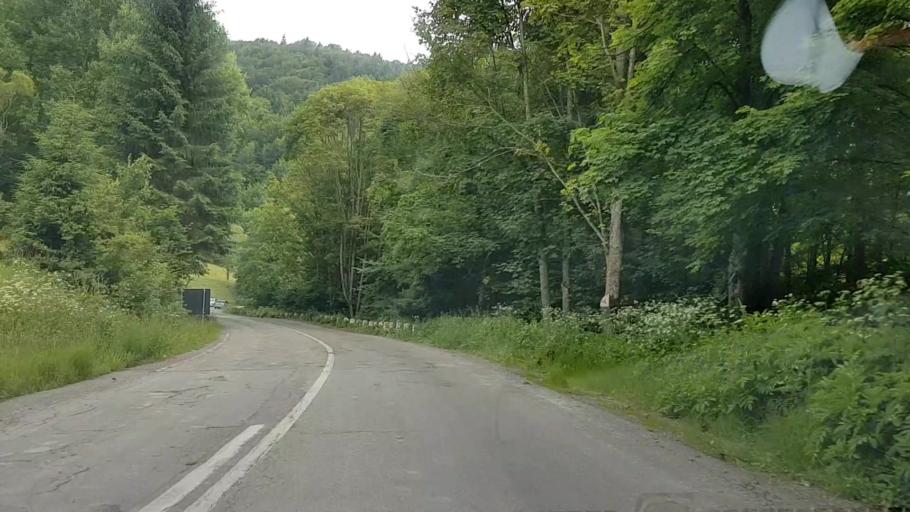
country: RO
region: Neamt
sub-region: Comuna Pangarati
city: Pangarati
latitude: 46.9367
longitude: 26.1265
